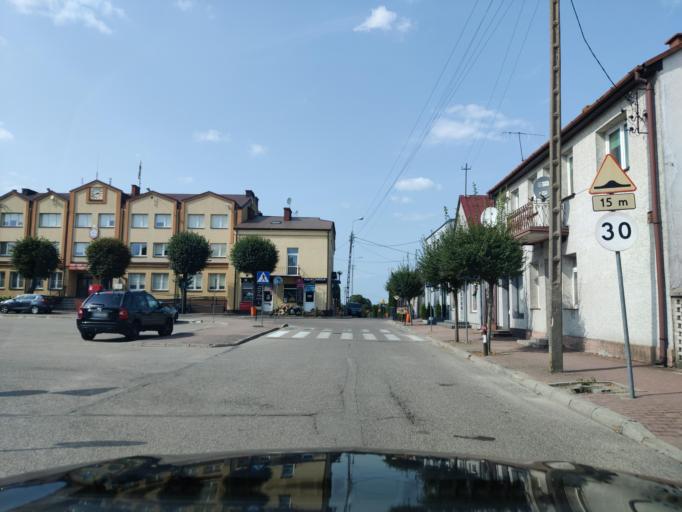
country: PL
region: Masovian Voivodeship
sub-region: Powiat makowski
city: Rozan
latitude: 52.8896
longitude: 21.3997
